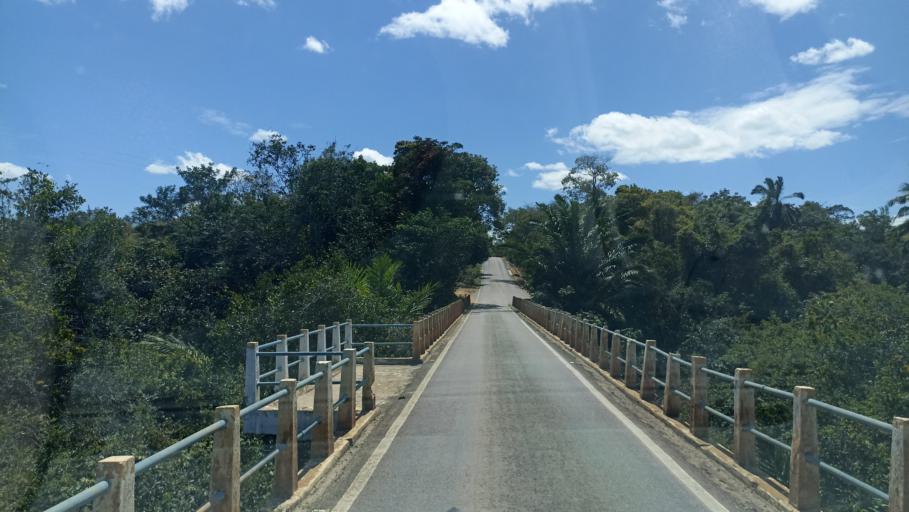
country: BR
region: Bahia
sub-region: Andarai
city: Vera Cruz
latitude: -12.7555
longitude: -41.3289
